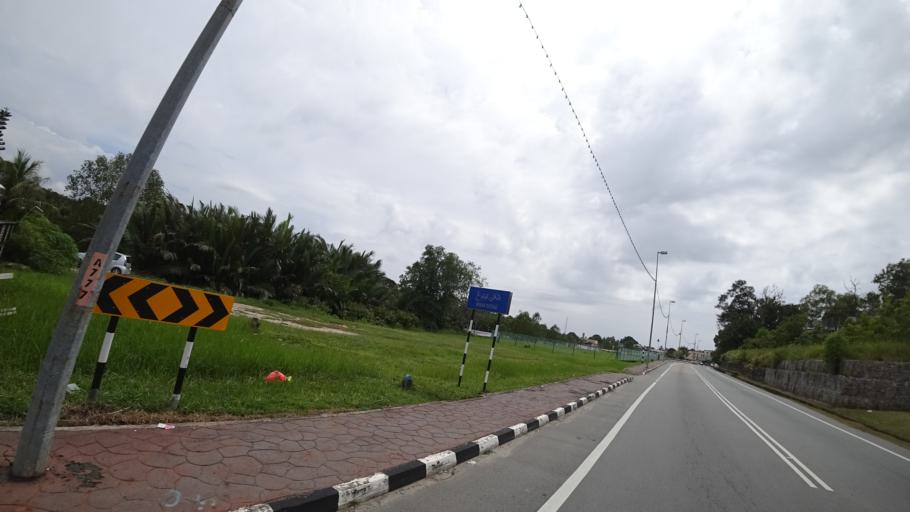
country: BN
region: Tutong
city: Tutong
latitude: 4.8056
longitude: 114.6612
